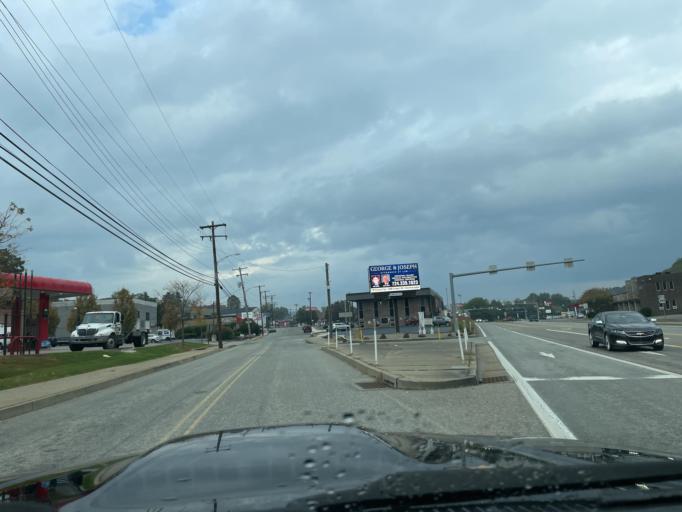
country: US
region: Pennsylvania
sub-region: Westmoreland County
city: Lower Burrell
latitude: 40.5552
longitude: -79.7590
